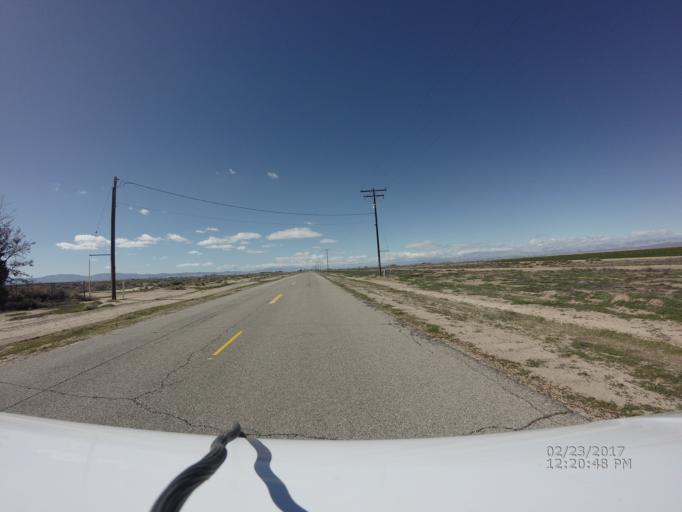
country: US
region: California
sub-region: Los Angeles County
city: Lancaster
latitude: 34.7489
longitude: -117.9752
